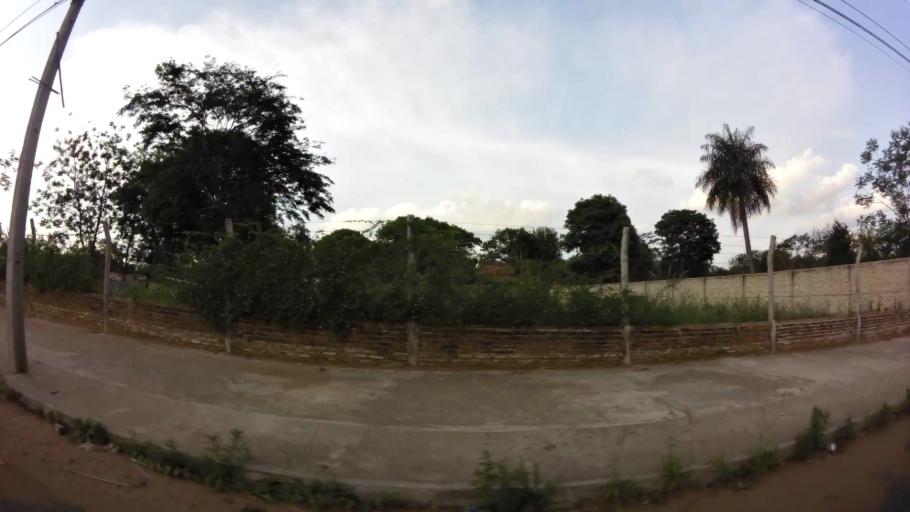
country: PY
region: Central
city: Nemby
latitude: -25.3701
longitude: -57.5259
